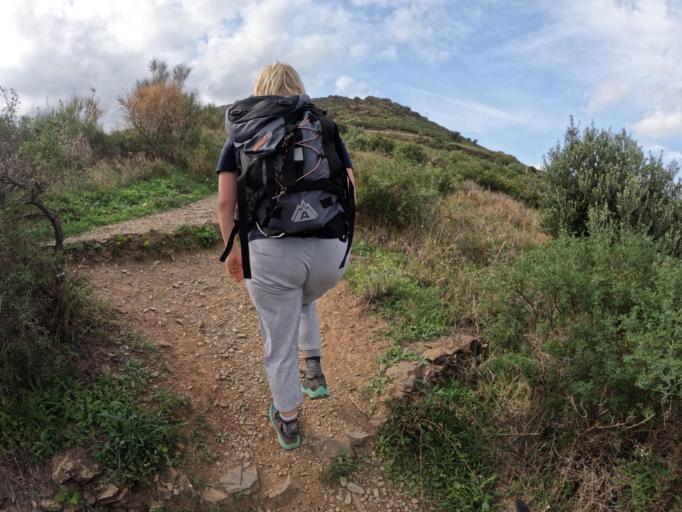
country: FR
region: Languedoc-Roussillon
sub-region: Departement des Pyrenees-Orientales
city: Cervera de la Marenda
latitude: 42.4533
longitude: 3.1601
